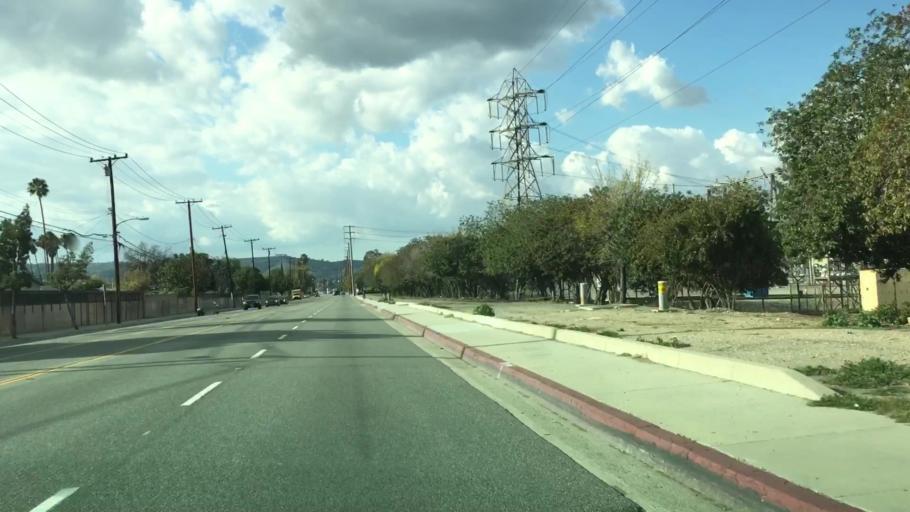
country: US
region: California
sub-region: Los Angeles County
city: La Puente
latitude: 34.0067
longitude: -117.9489
